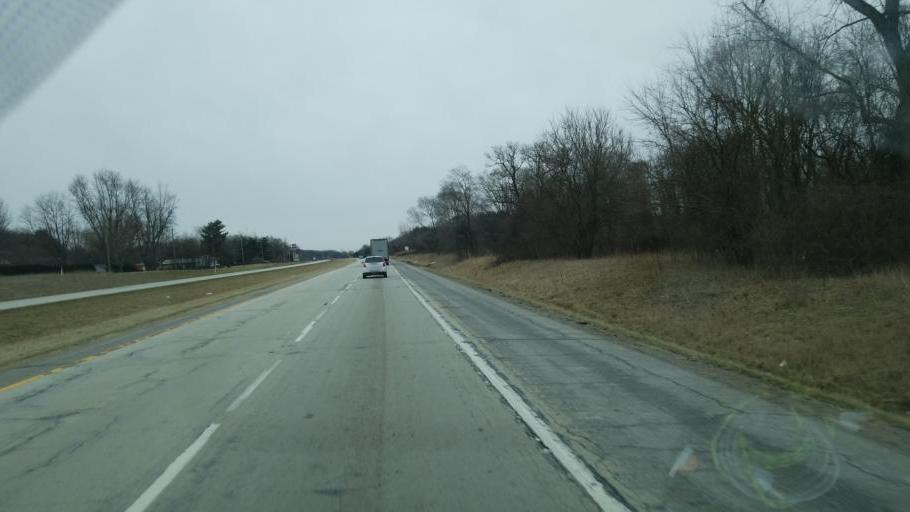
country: US
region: Indiana
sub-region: Starke County
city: Koontz Lake
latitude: 41.3704
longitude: -86.5013
